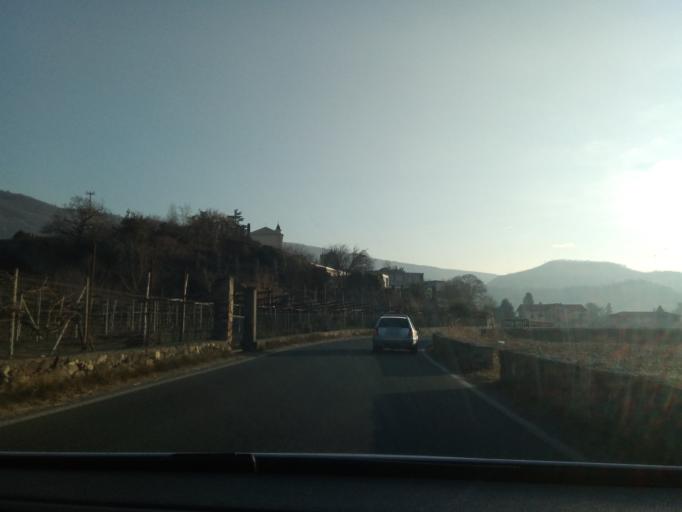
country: IT
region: Piedmont
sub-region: Provincia di Torino
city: Borgofranco d'Ivrea
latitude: 45.5097
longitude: 7.8510
